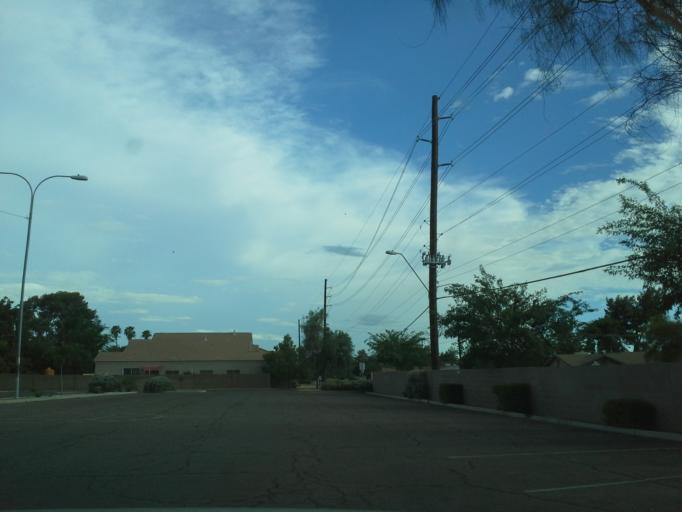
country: US
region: Arizona
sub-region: Maricopa County
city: Phoenix
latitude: 33.5369
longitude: -112.0910
